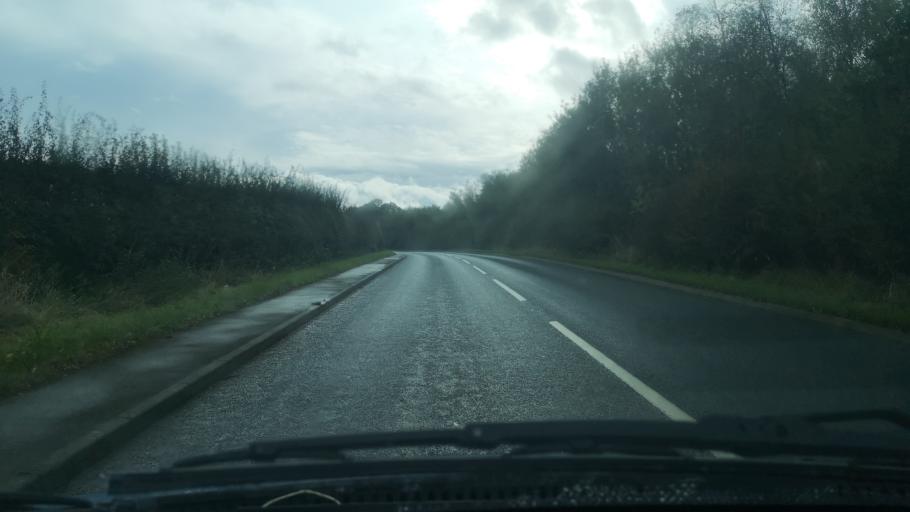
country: GB
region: England
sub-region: City and Borough of Wakefield
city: Fitzwilliam
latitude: 53.6445
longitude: -1.3866
